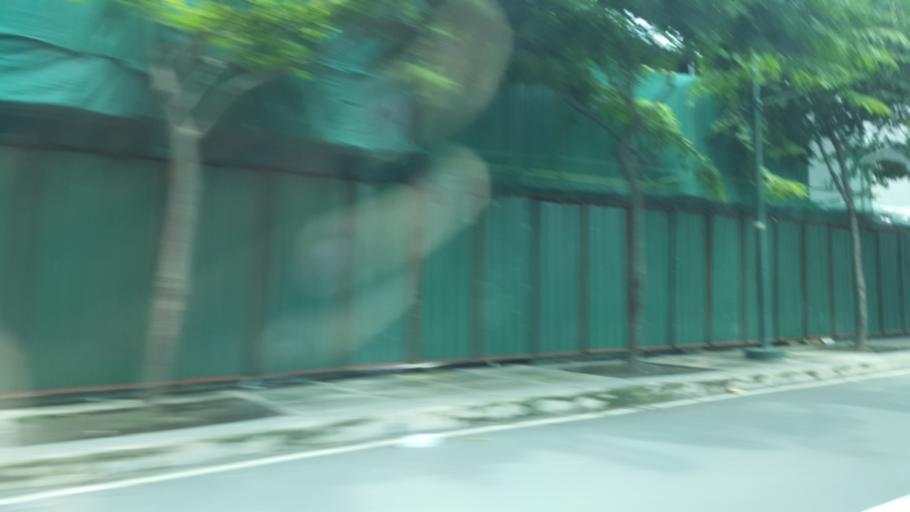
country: PH
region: Calabarzon
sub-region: Province of Rizal
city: Pateros
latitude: 14.5524
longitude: 121.0557
